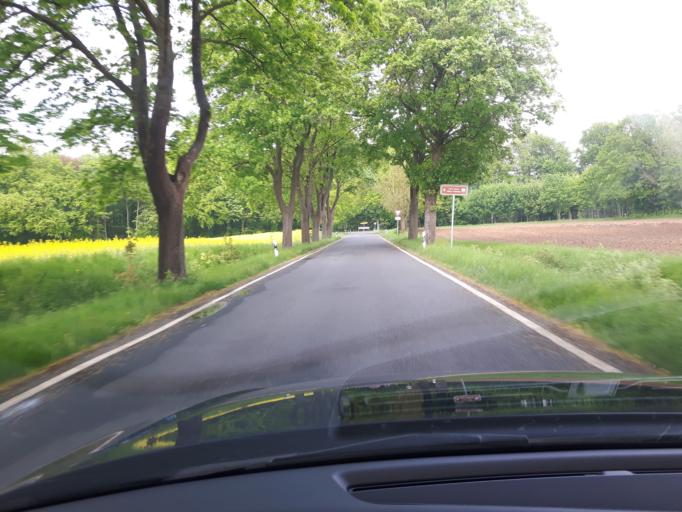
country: DE
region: Mecklenburg-Vorpommern
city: Velgast
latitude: 54.2278
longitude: 12.7322
